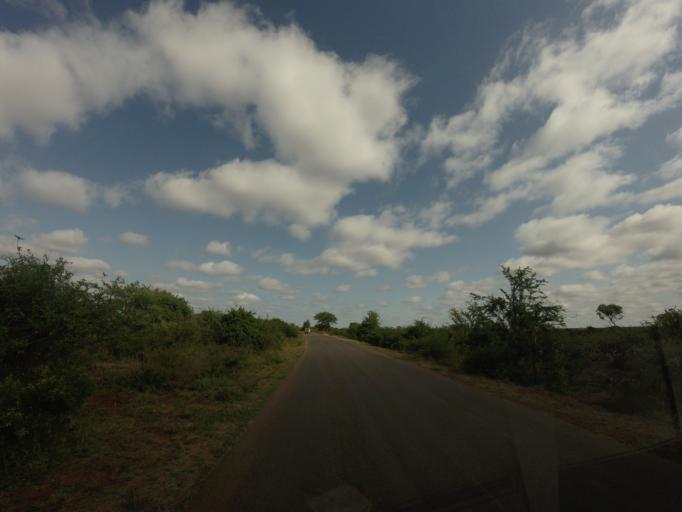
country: ZA
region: Mpumalanga
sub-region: Ehlanzeni District
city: Komatipoort
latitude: -25.1301
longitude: 31.9427
